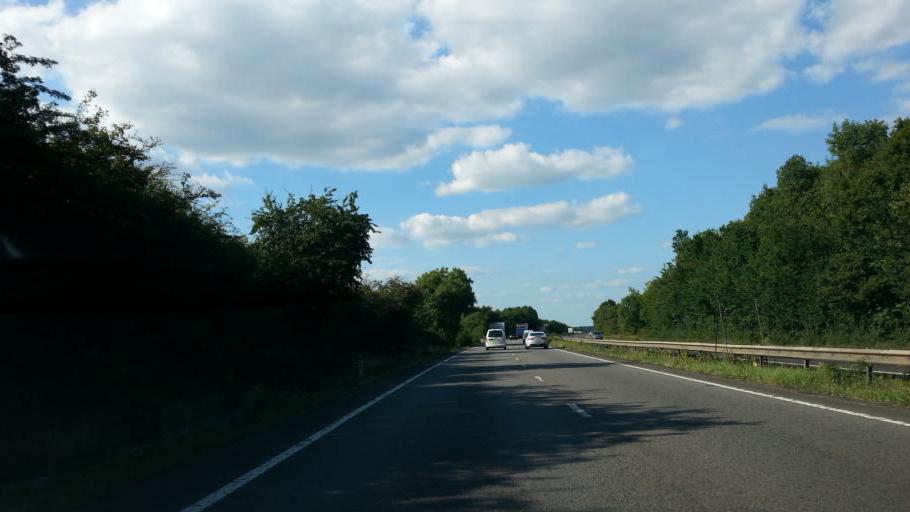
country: GB
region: England
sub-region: Lincolnshire
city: Great Gonerby
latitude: 52.9356
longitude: -0.6851
